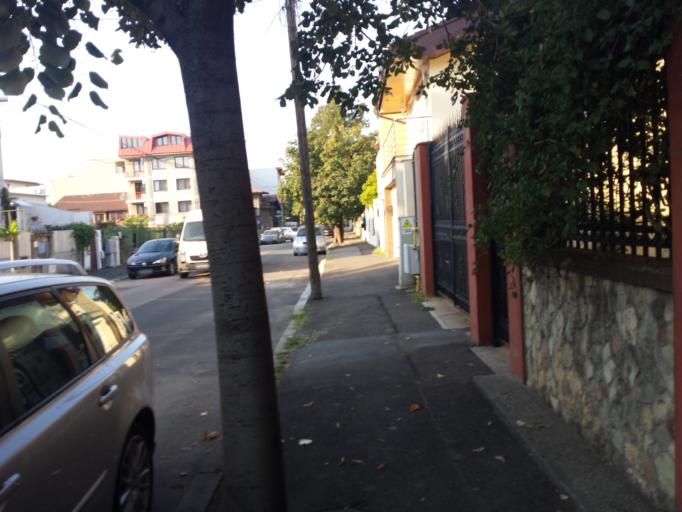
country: RO
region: Bucuresti
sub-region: Municipiul Bucuresti
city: Bucuresti
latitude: 44.4637
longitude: 26.0648
